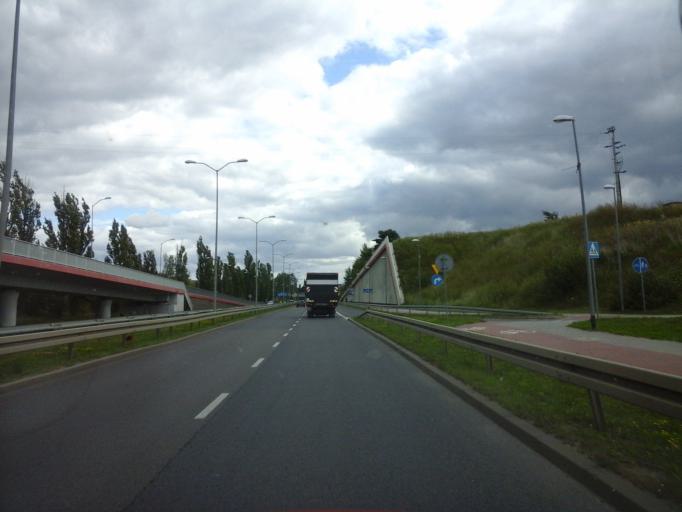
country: PL
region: West Pomeranian Voivodeship
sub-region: Powiat policki
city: Przeclaw
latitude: 53.3889
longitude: 14.5096
